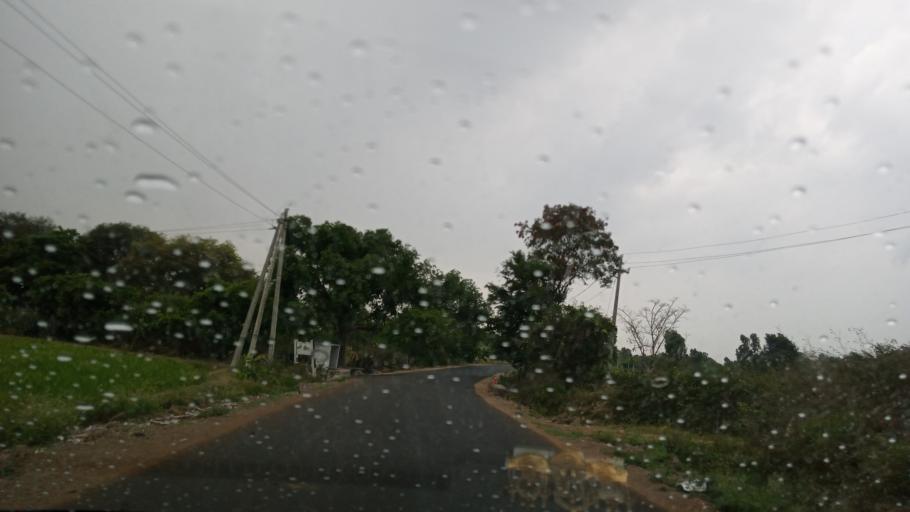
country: IN
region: Karnataka
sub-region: Kolar
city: Mulbagal
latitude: 13.1051
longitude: 78.3265
